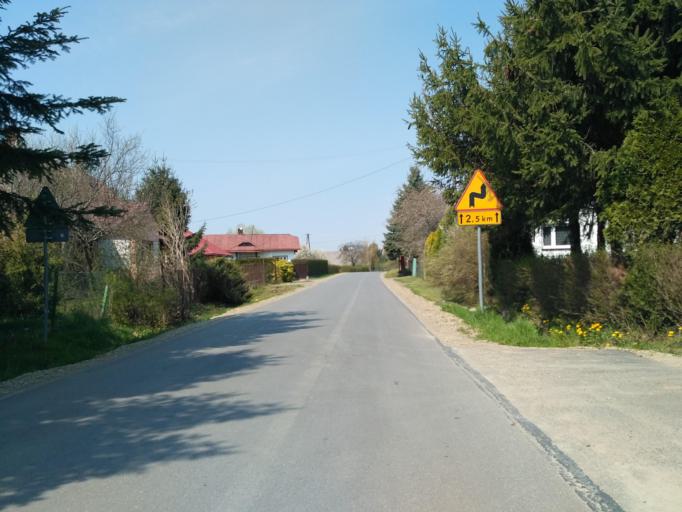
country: PL
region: Subcarpathian Voivodeship
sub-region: Powiat krosnienski
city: Chorkowka
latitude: 49.6331
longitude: 21.6985
